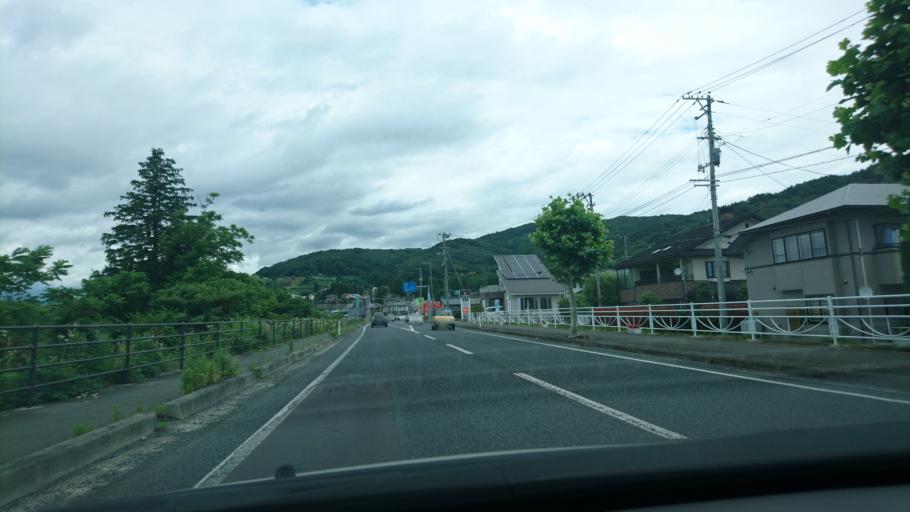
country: JP
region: Iwate
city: Morioka-shi
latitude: 39.6548
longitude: 141.1823
